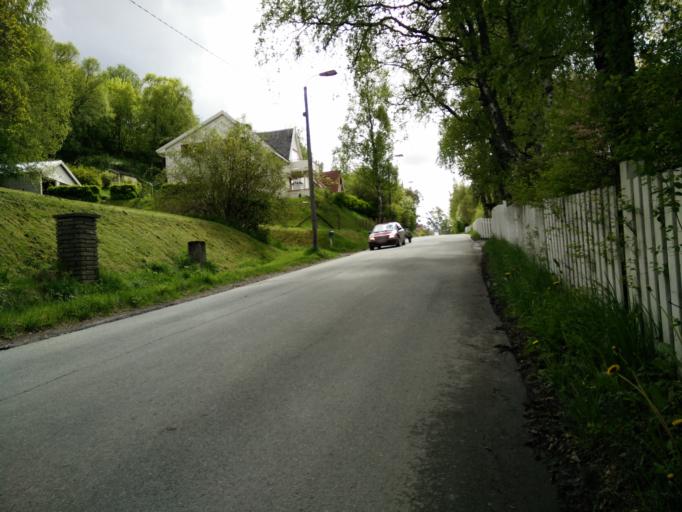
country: NO
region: Sor-Trondelag
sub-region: Trondheim
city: Trondheim
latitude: 63.4069
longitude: 10.4041
